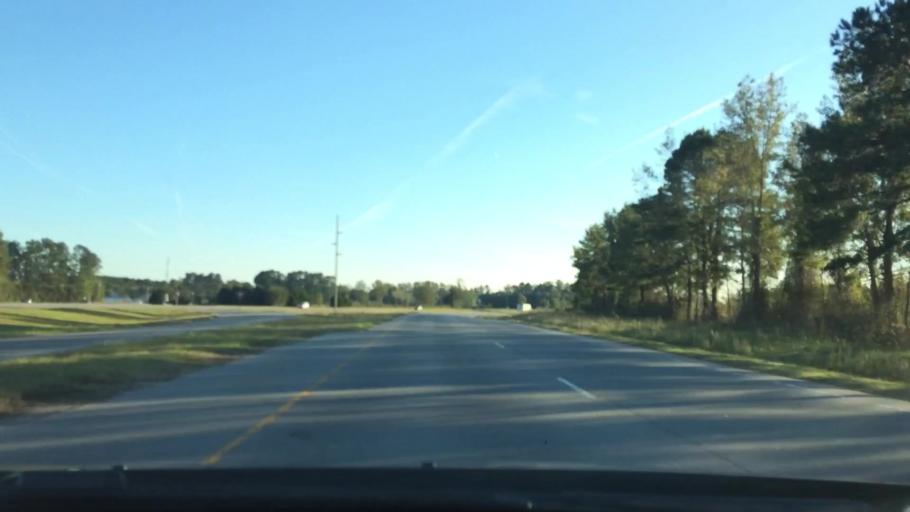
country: US
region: North Carolina
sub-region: Pitt County
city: Grifton
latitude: 35.4060
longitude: -77.4361
